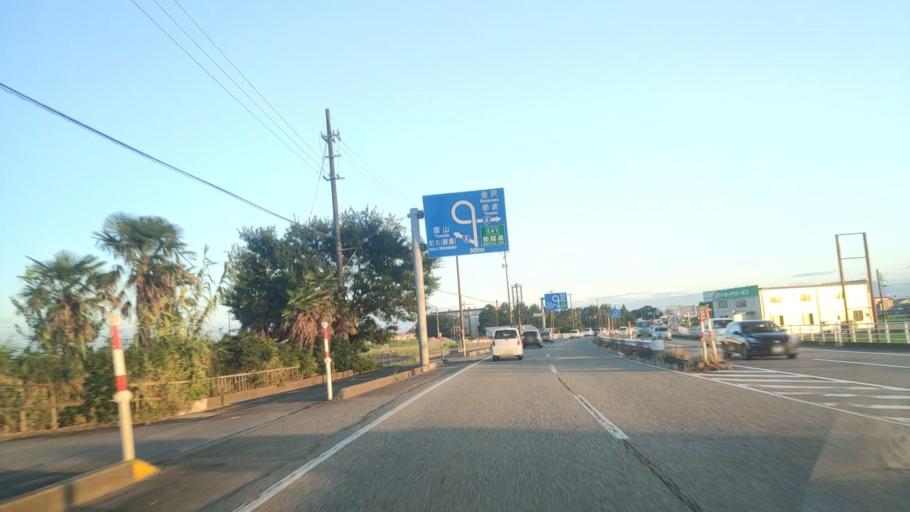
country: JP
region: Toyama
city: Takaoka
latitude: 36.7666
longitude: 137.0052
